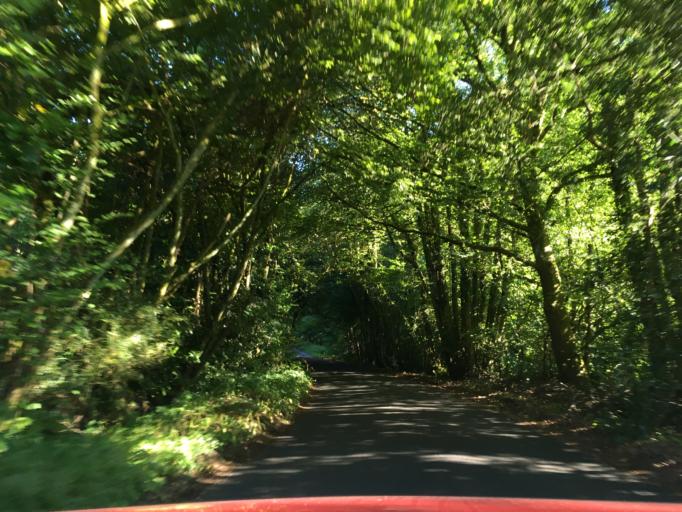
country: GB
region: Wales
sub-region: Monmouthshire
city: Tintern
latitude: 51.7199
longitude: -2.6907
